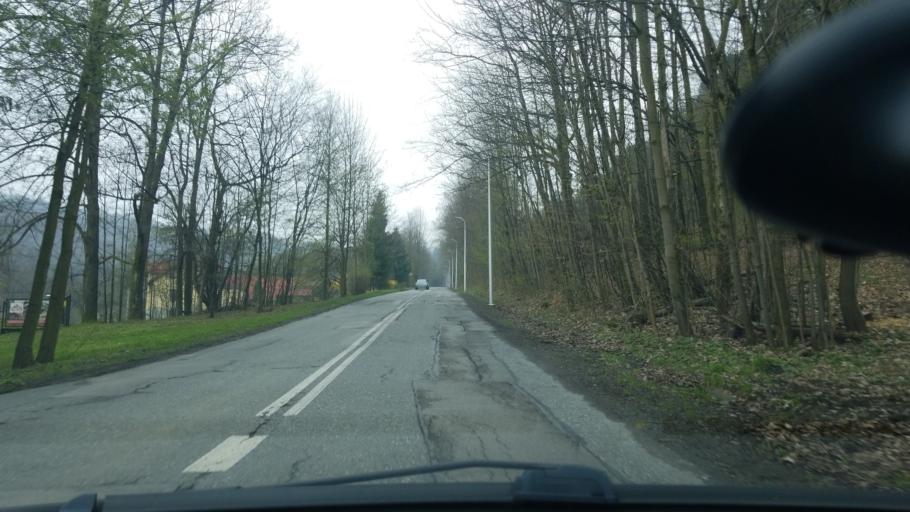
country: PL
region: Silesian Voivodeship
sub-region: Powiat cieszynski
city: Ustron
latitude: 49.7071
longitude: 18.8271
